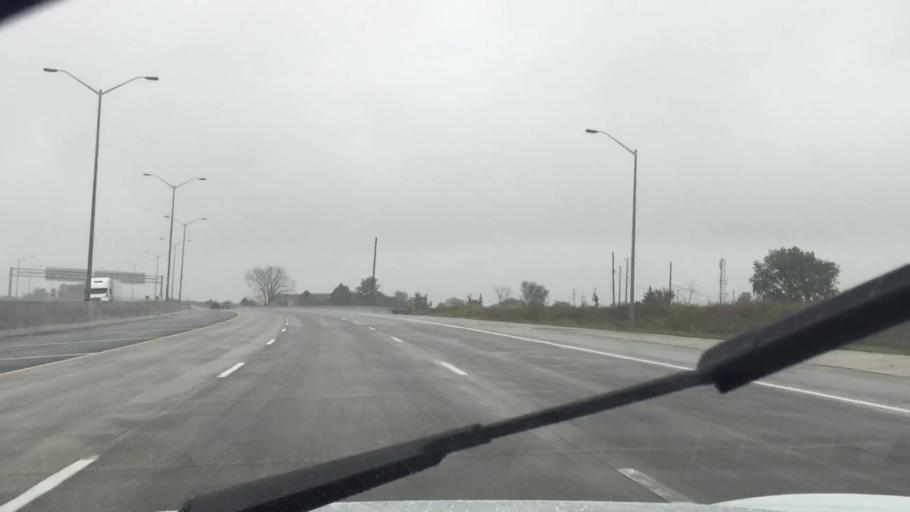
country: CA
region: Ontario
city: Windsor
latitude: 42.2332
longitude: -82.9886
